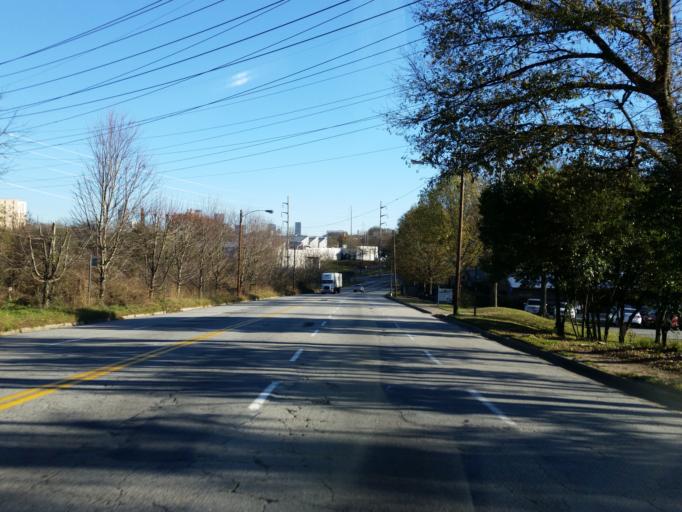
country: US
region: Georgia
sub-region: Fulton County
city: Atlanta
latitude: 33.7798
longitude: -84.4286
